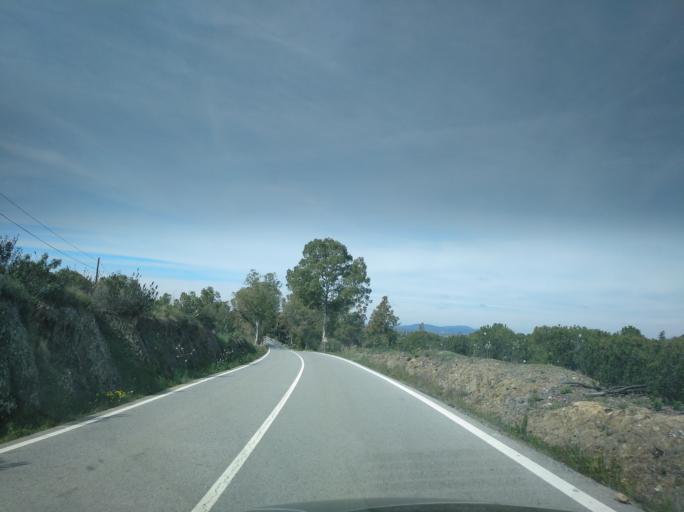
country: PT
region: Beja
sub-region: Mertola
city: Mertola
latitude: 37.5669
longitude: -7.6691
